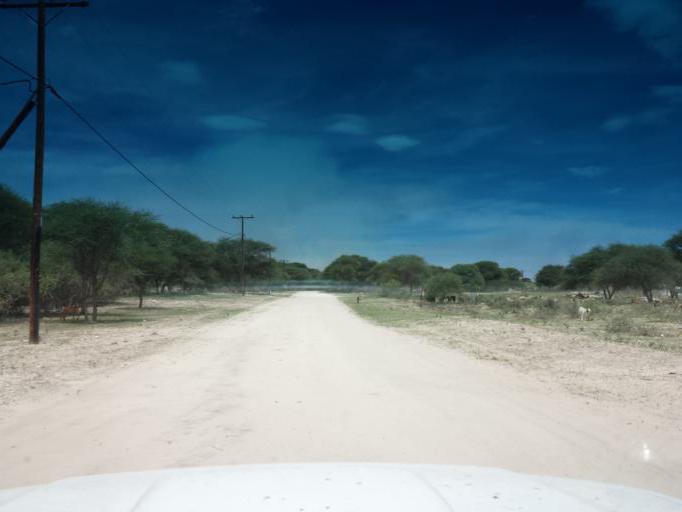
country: BW
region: North West
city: Shakawe
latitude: -18.7423
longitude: 22.1784
